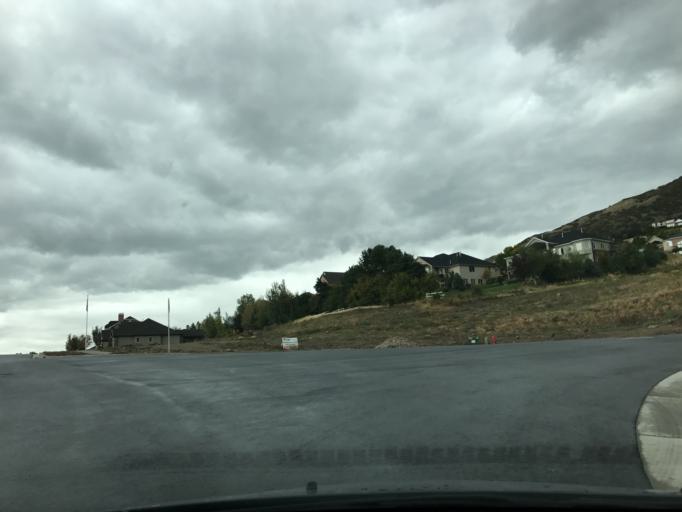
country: US
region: Utah
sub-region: Davis County
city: Fruit Heights
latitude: 41.0064
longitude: -111.8956
